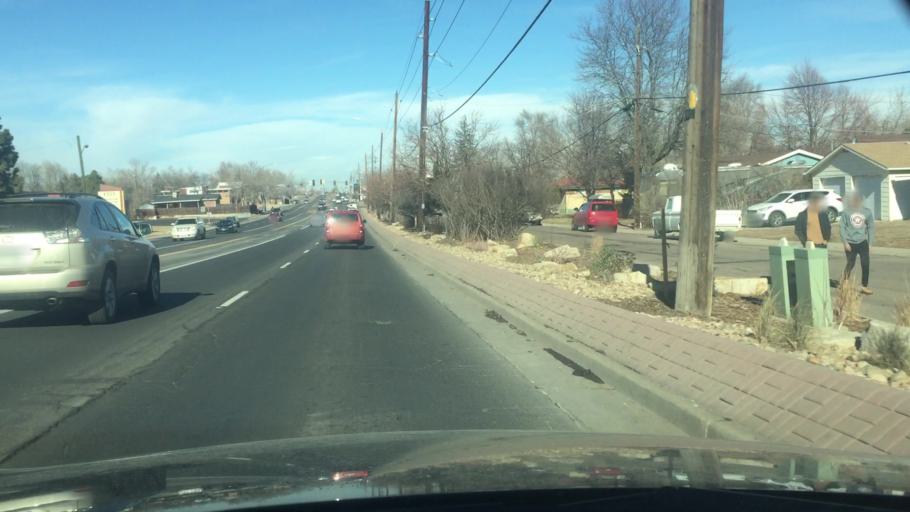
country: US
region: Colorado
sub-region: Jefferson County
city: Lakewood
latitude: 39.6872
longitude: -105.0814
